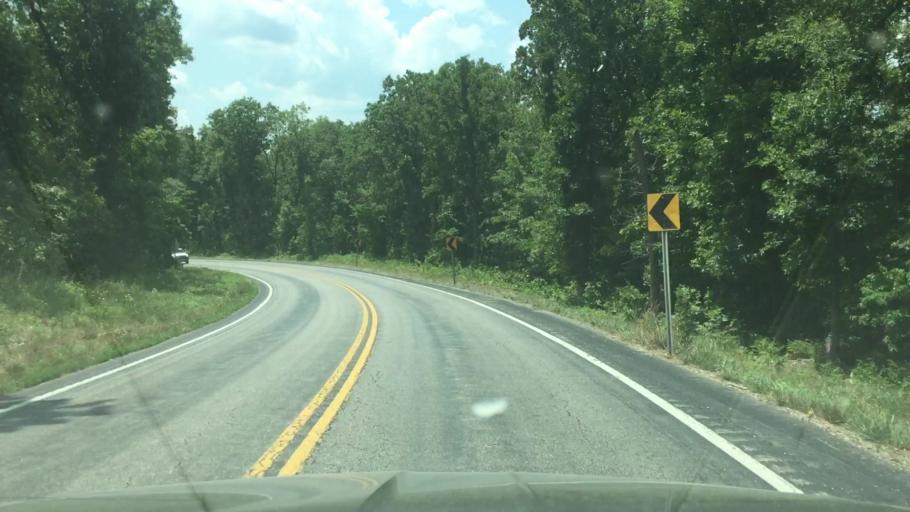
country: US
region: Missouri
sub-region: Camden County
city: Osage Beach
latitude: 38.1277
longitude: -92.5576
